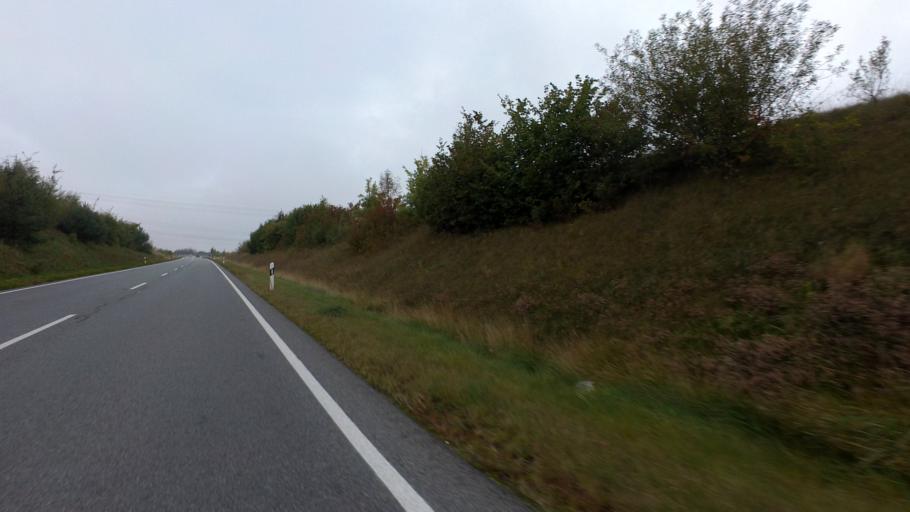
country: DE
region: Saxony
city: Berthelsdorf
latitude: 51.0758
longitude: 14.1937
